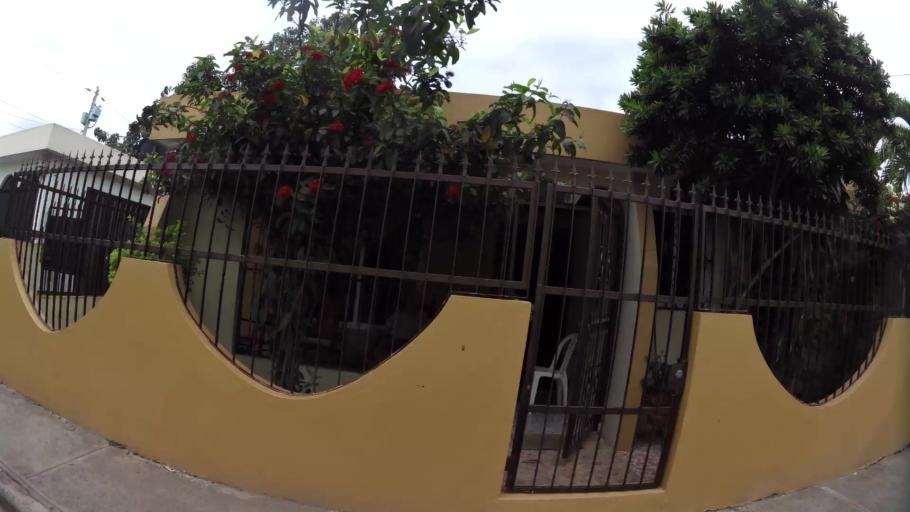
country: DO
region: Santiago
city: Santiago de los Caballeros
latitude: 19.4295
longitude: -70.6674
